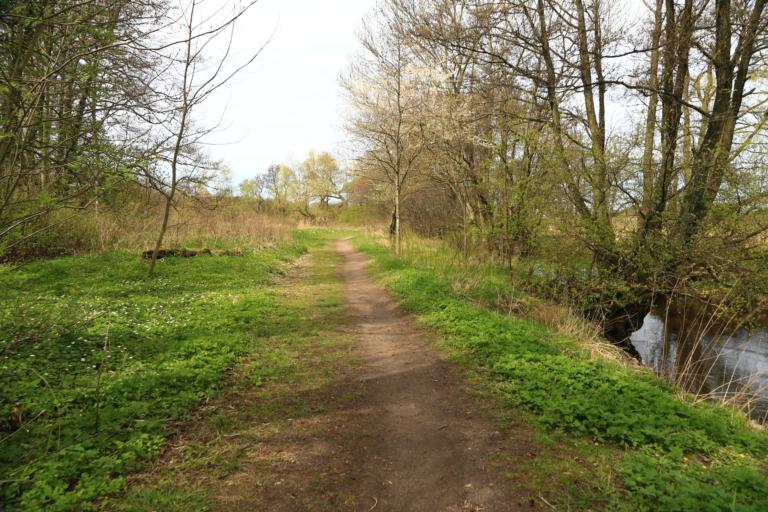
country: SE
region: Halland
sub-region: Varbergs Kommun
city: Varberg
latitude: 57.1295
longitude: 12.2851
